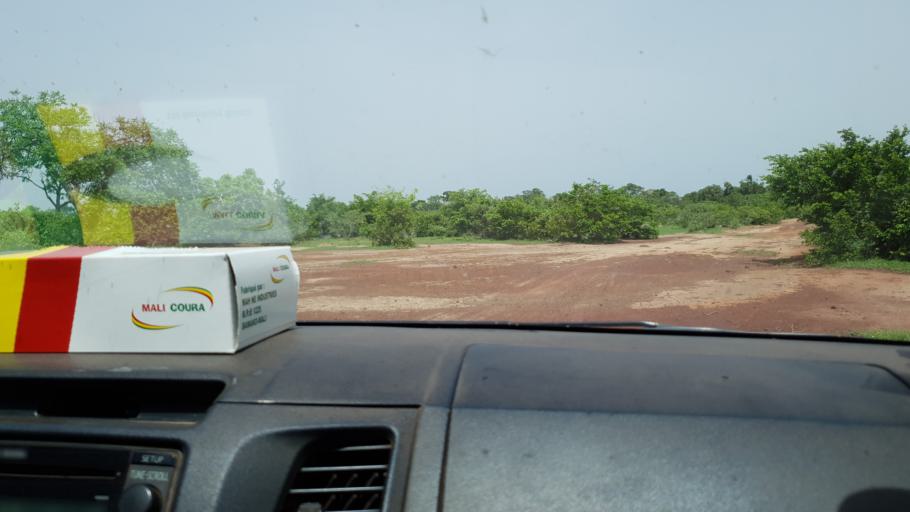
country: ML
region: Koulikoro
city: Koulikoro
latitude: 12.6667
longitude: -7.2380
